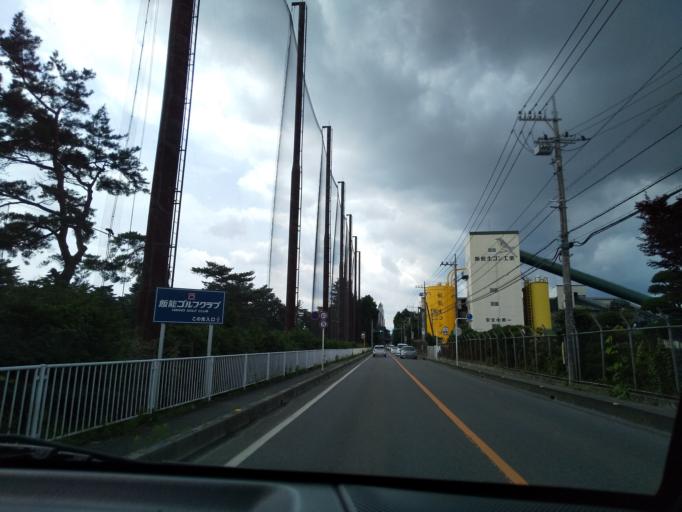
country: JP
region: Saitama
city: Hanno
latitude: 35.8626
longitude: 139.3635
